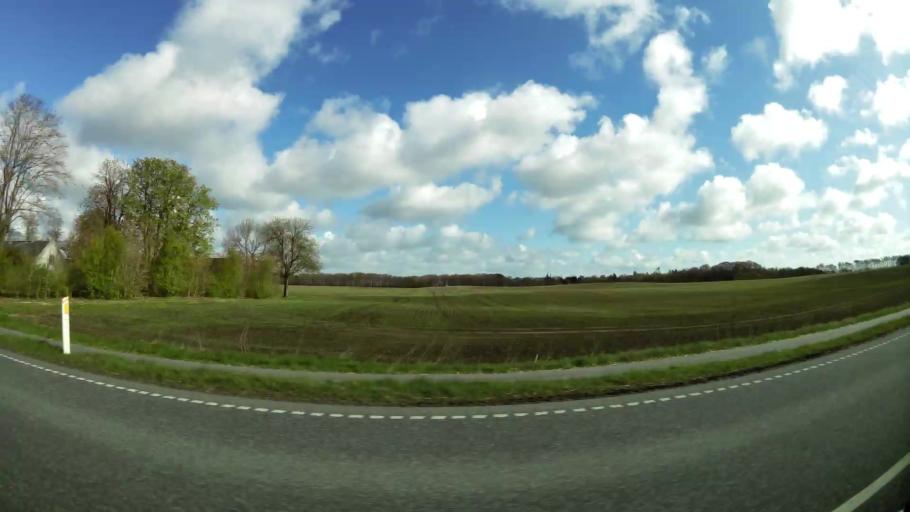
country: DK
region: North Denmark
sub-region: Mariagerfjord Kommune
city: Hobro
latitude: 56.6261
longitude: 9.8360
